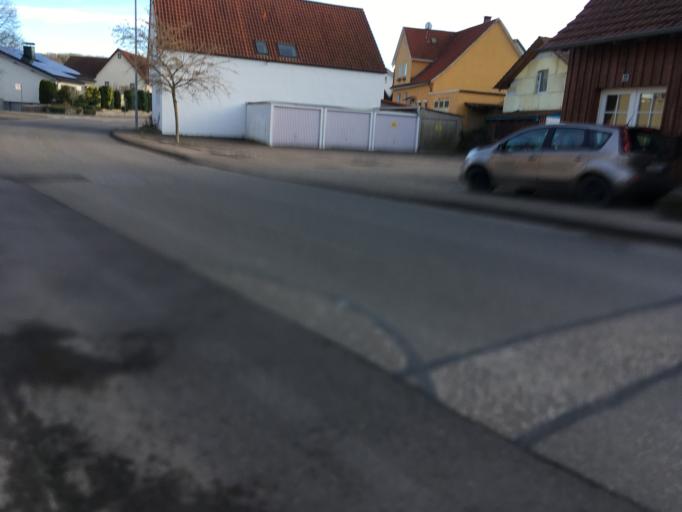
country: DE
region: Baden-Wuerttemberg
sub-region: Regierungsbezirk Stuttgart
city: Lehrensteinsfeld
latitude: 49.1283
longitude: 9.3259
